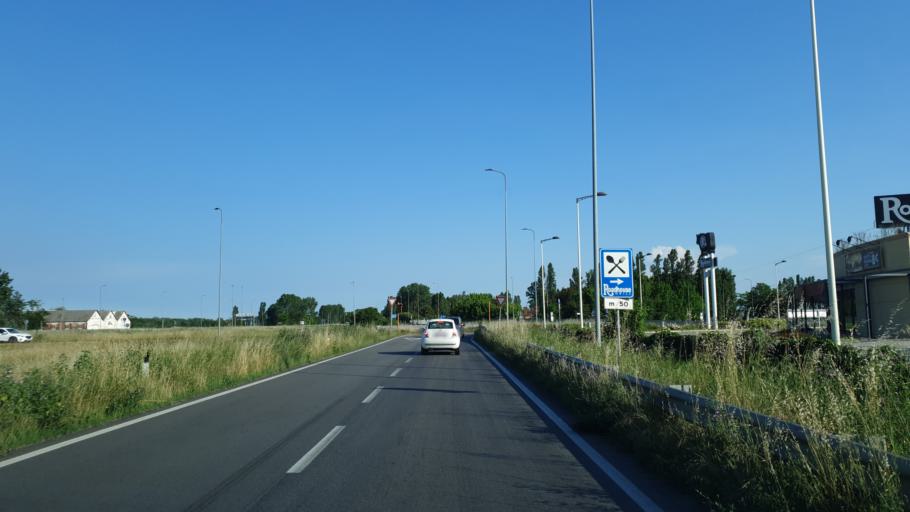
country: IT
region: Emilia-Romagna
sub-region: Provincia di Ravenna
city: Fosso Ghiaia
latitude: 44.3350
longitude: 12.2707
